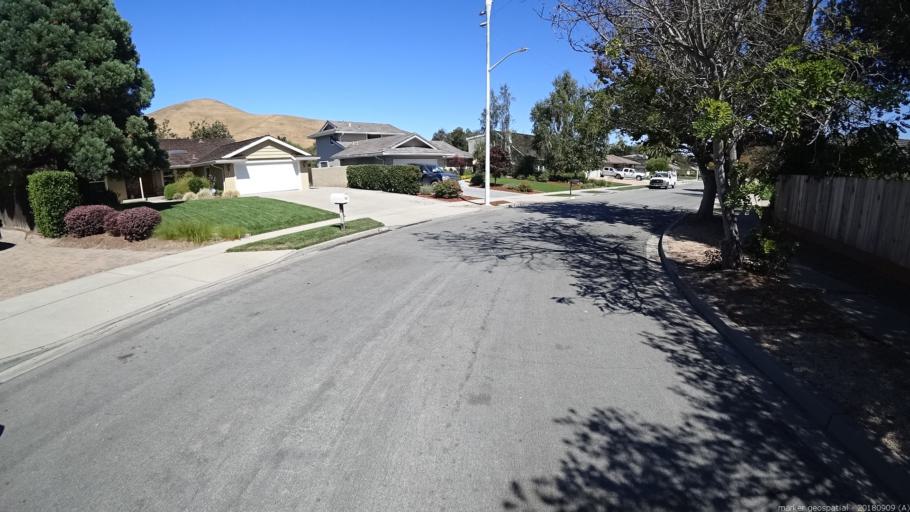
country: US
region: California
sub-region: Monterey County
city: Salinas
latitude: 36.6038
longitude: -121.6991
